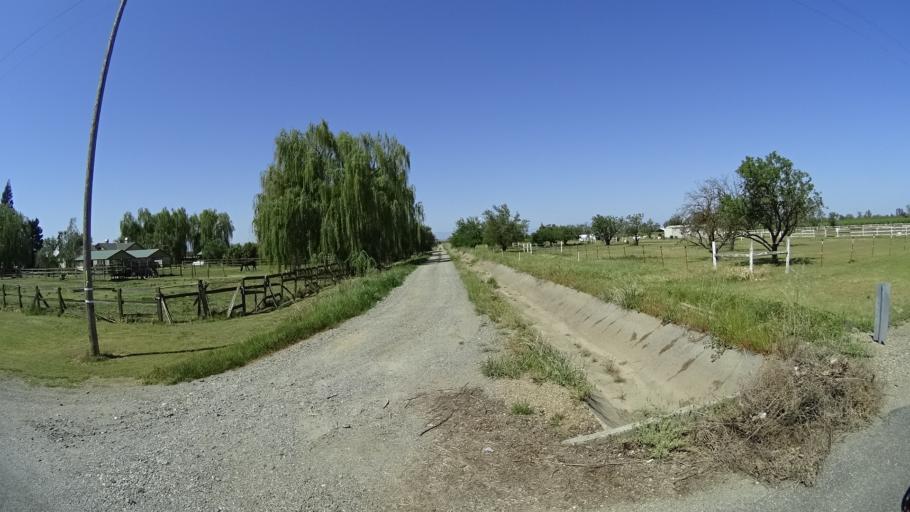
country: US
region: California
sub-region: Glenn County
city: Orland
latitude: 39.7823
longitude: -122.1597
